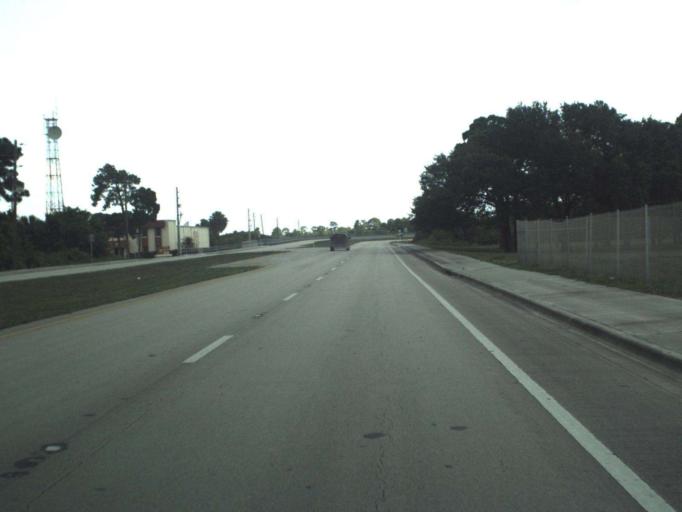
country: US
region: Florida
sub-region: Saint Lucie County
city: Fort Pierce North
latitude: 27.4924
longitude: -80.3496
